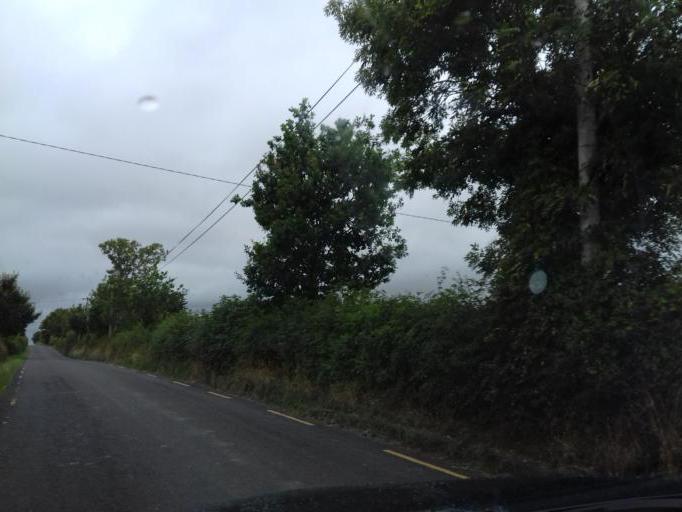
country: IE
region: Leinster
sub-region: Kilkenny
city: Graiguenamanagh
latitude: 52.6169
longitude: -7.0358
